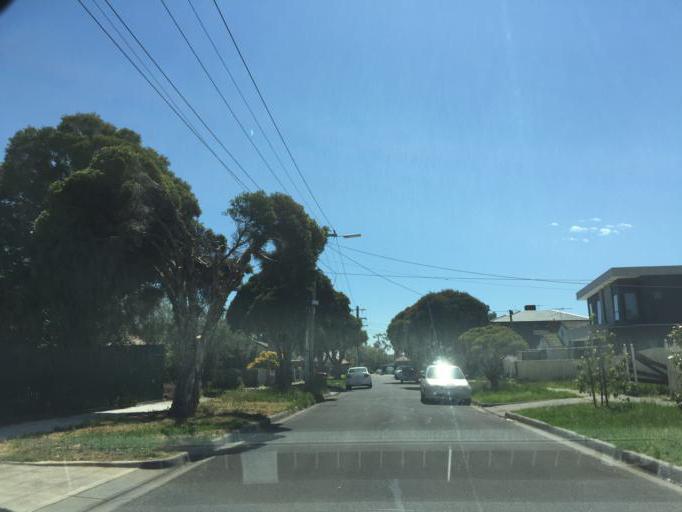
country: AU
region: Victoria
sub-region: Maribyrnong
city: Braybrook
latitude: -37.7889
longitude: 144.8478
